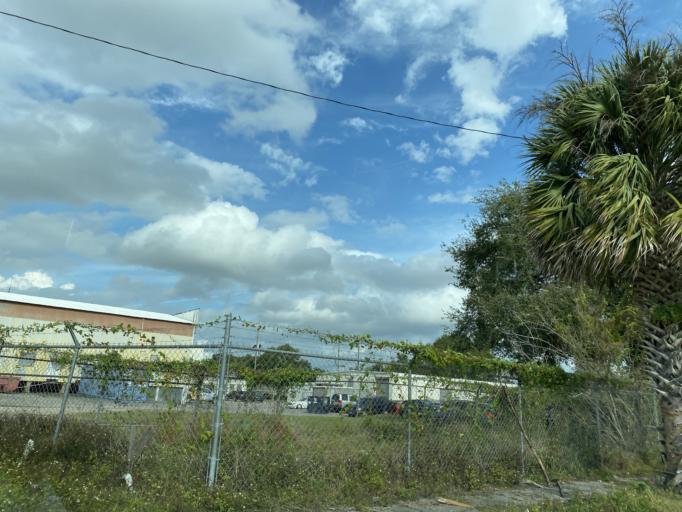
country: US
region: Florida
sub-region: Orange County
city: Orlando
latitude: 28.5483
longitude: -81.3952
